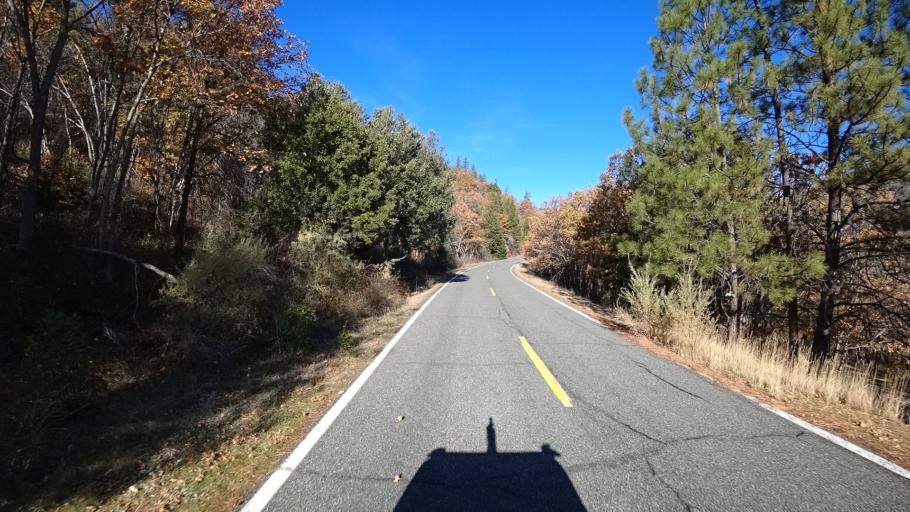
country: US
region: California
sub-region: Siskiyou County
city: Yreka
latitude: 41.9002
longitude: -122.8291
